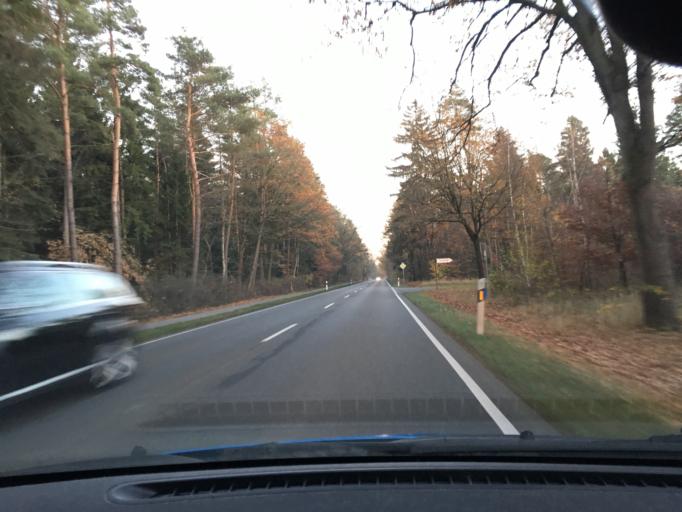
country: DE
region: Lower Saxony
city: Schwienau
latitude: 52.9992
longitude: 10.4760
